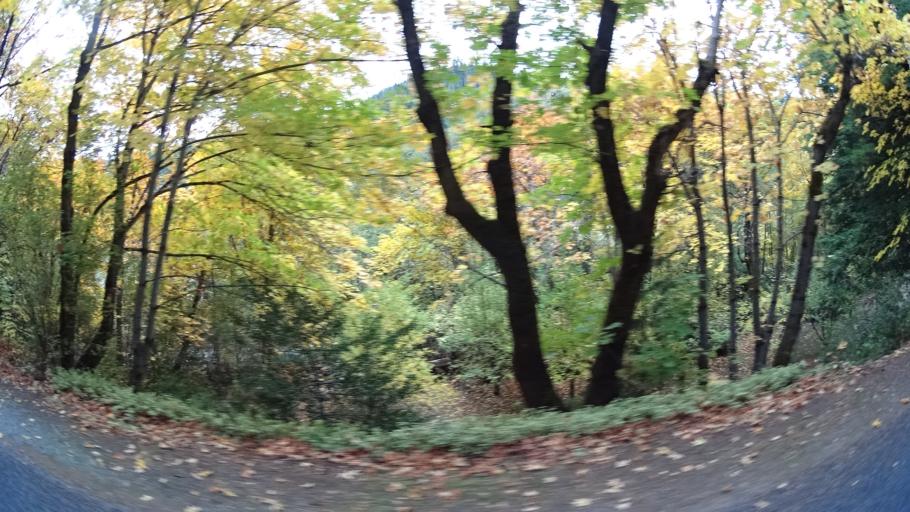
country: US
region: California
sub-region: Siskiyou County
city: Happy Camp
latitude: 41.8656
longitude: -123.1418
